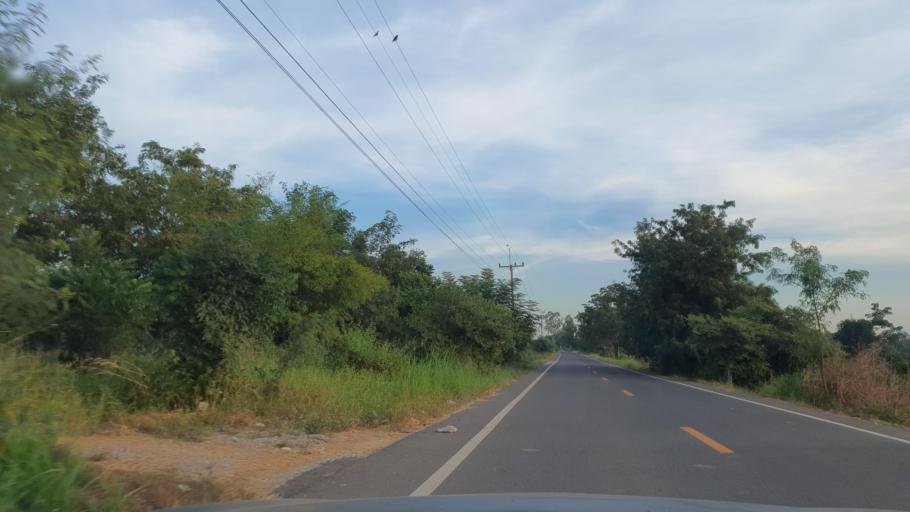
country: TH
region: Uthai Thani
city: Sawang Arom
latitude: 15.7147
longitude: 99.9522
